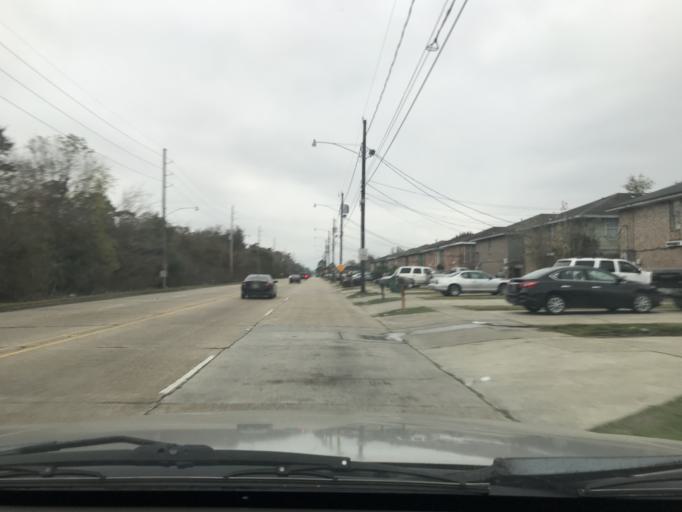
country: US
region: Louisiana
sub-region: Jefferson Parish
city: Woodmere
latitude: 29.8637
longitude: -90.0736
